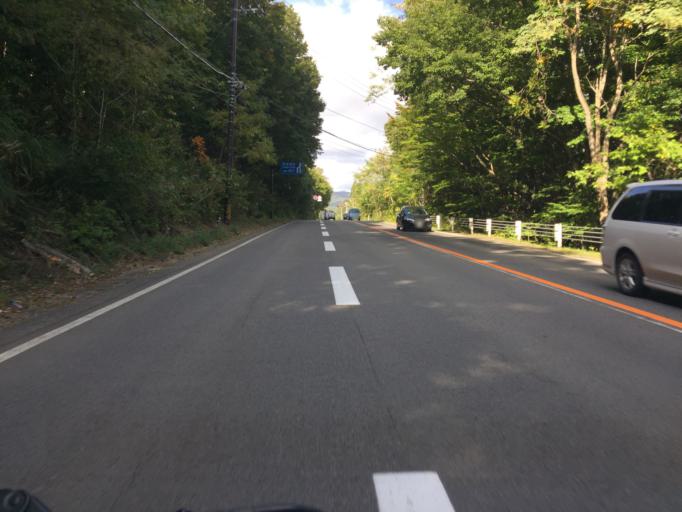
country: JP
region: Fukushima
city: Inawashiro
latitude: 37.6253
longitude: 140.2091
